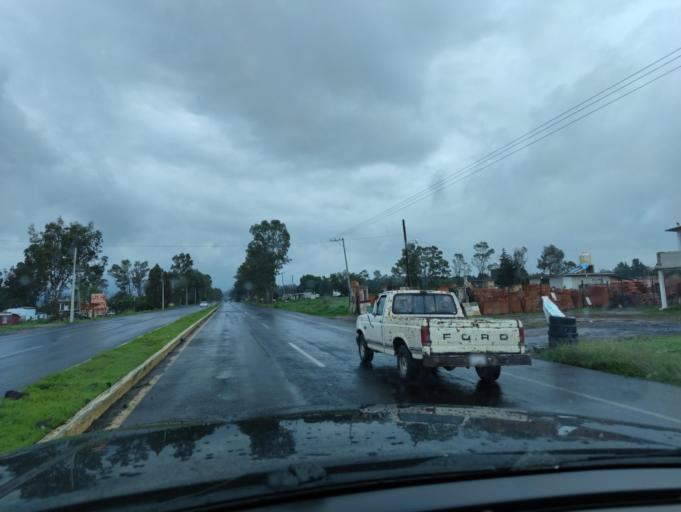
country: MX
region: Mexico
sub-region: Jilotepec
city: Doxhicho
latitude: 19.9172
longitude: -99.5978
